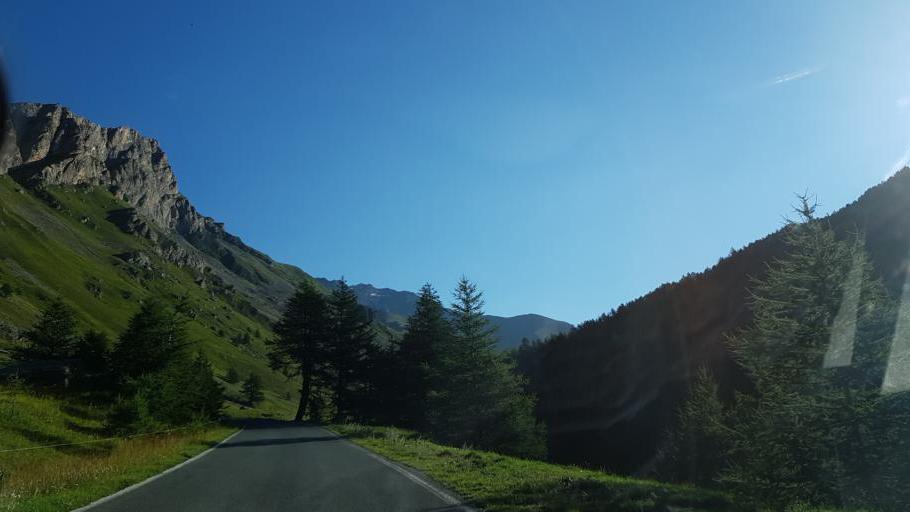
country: IT
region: Piedmont
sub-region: Provincia di Cuneo
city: Pontechianale
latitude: 44.6592
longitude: 6.9906
